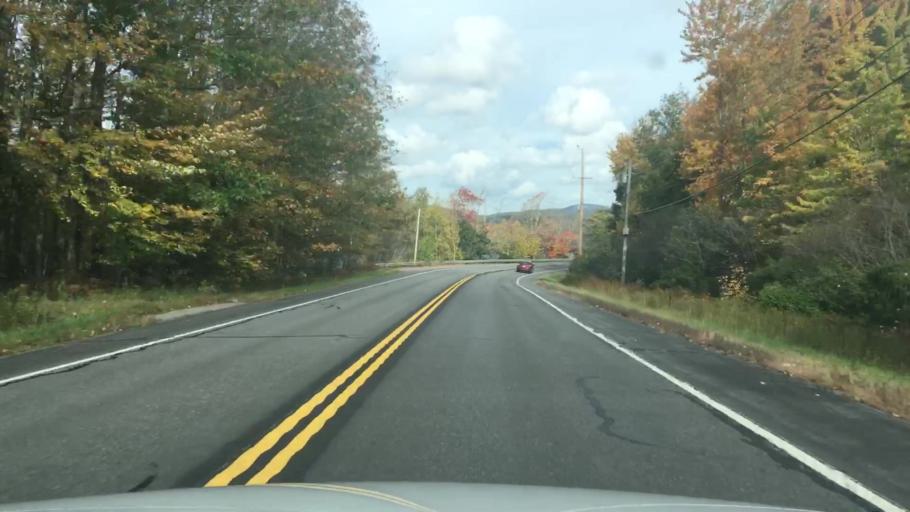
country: US
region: Maine
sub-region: Knox County
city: Rockport
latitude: 44.1658
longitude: -69.1194
